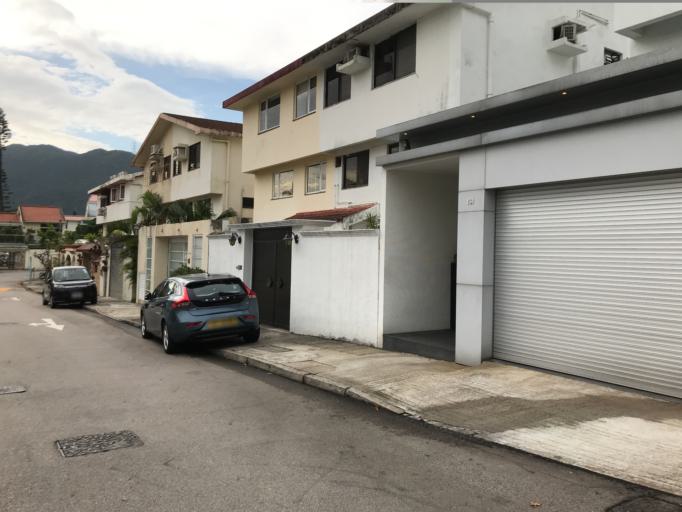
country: HK
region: Tai Po
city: Tai Po
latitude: 22.4647
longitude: 114.1556
